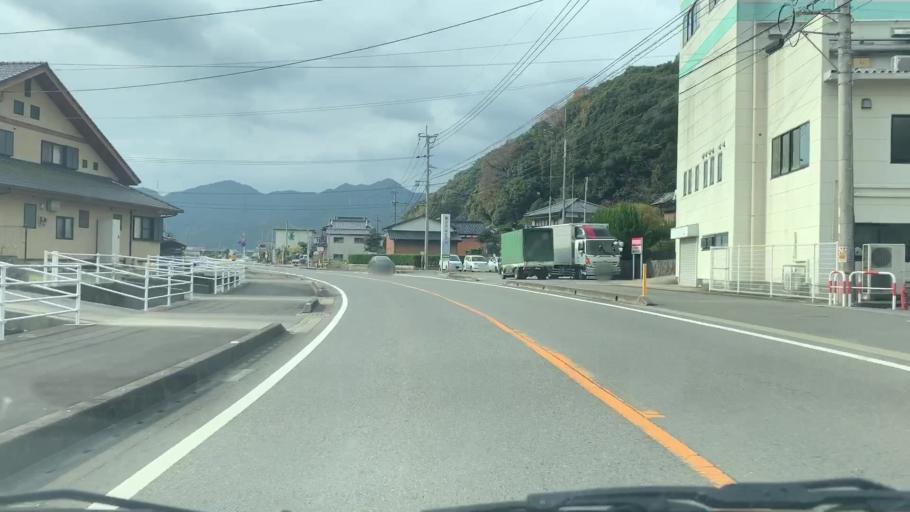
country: JP
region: Saga Prefecture
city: Kashima
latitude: 33.1284
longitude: 130.0517
